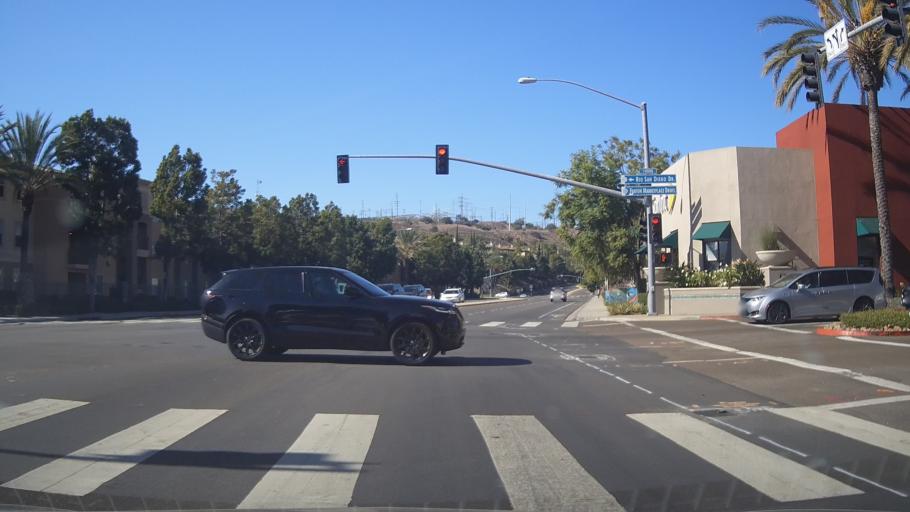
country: US
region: California
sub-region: San Diego County
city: San Diego
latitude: 32.7798
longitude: -117.1296
